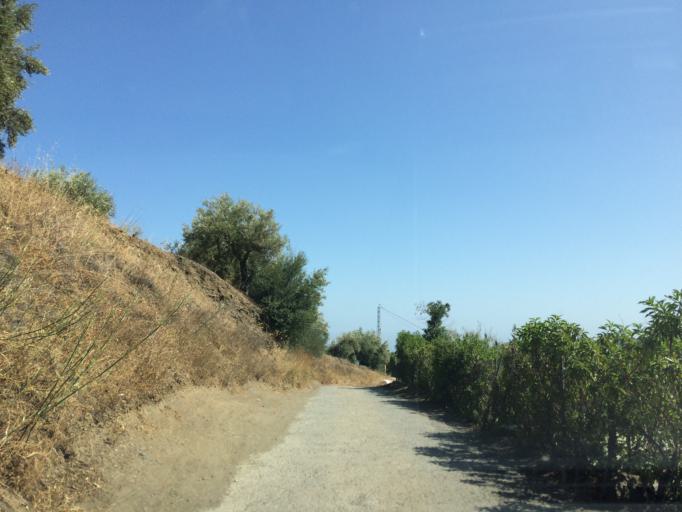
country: ES
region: Andalusia
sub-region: Provincia de Malaga
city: Frigiliana
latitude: 36.7980
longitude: -3.9106
